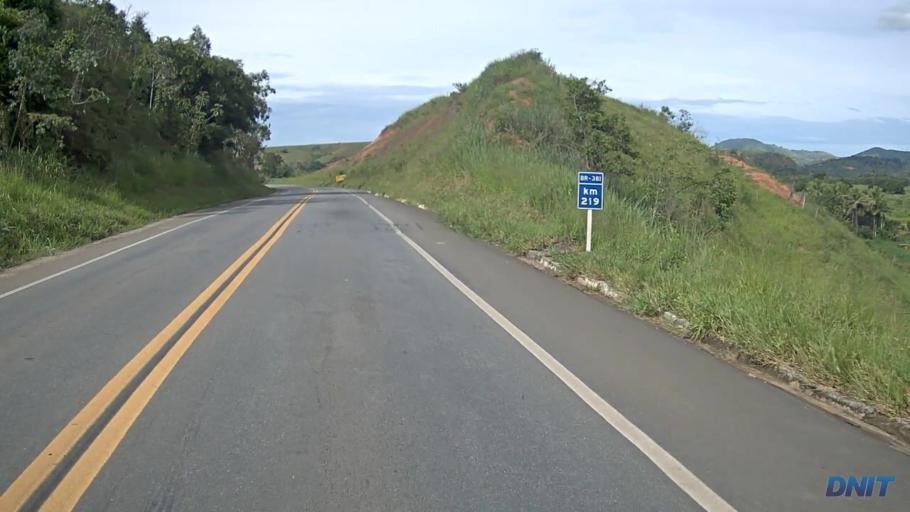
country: BR
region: Minas Gerais
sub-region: Belo Oriente
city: Belo Oriente
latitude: -19.2622
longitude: -42.3446
